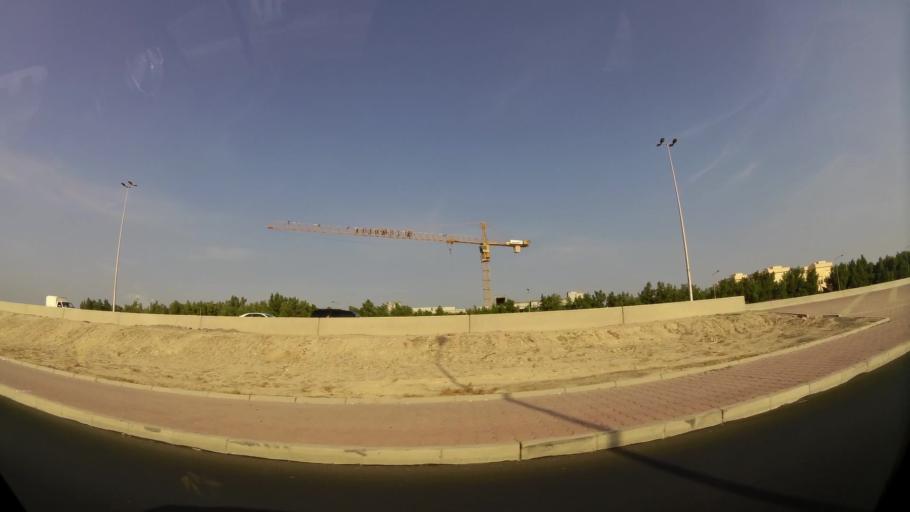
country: KW
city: Al Funaytis
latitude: 29.2088
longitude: 48.1040
